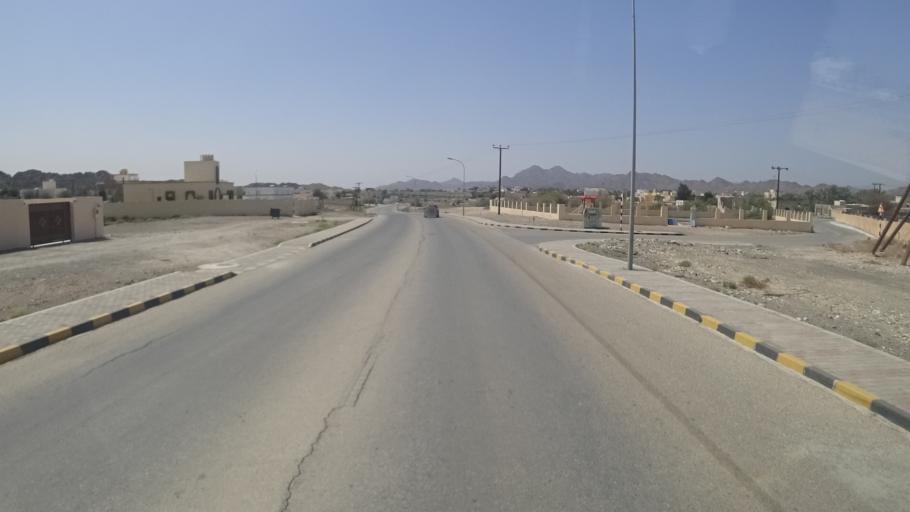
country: OM
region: Ash Sharqiyah
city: Ibra'
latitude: 22.6817
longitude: 58.5411
